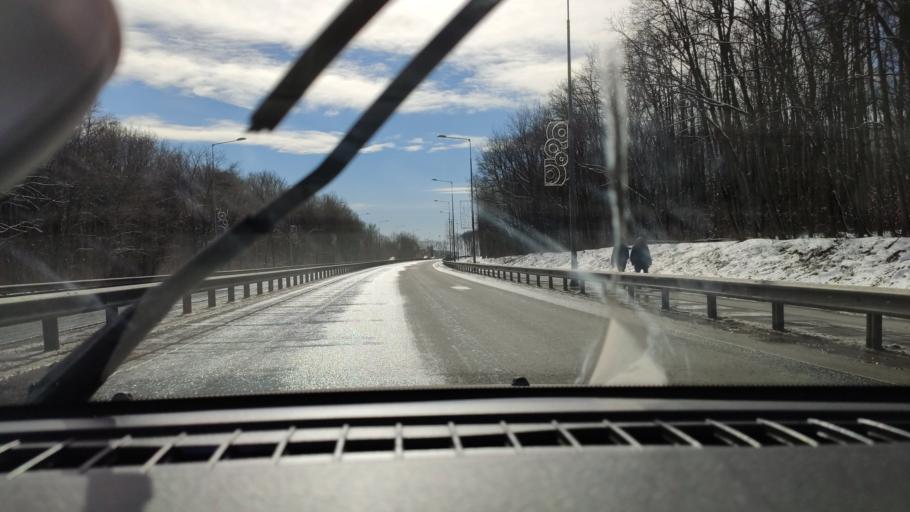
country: RU
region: Samara
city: Petra-Dubrava
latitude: 53.2844
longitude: 50.2509
